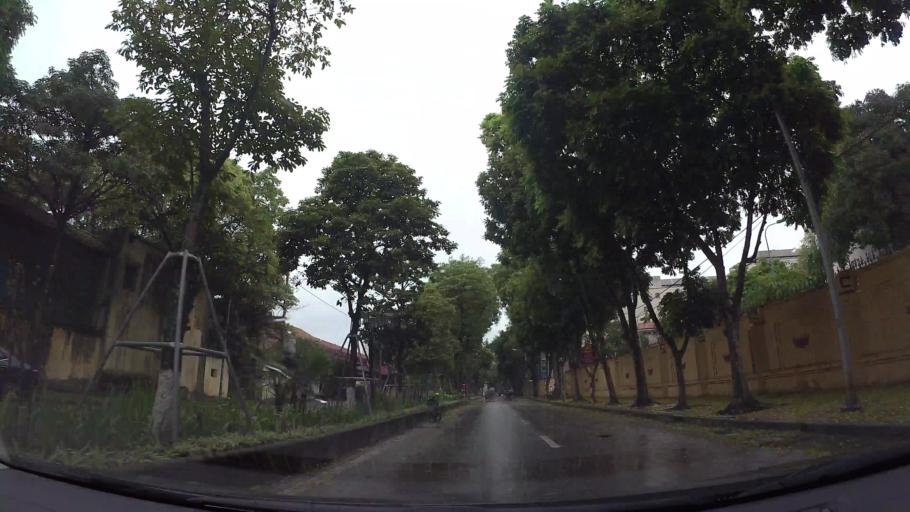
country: VN
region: Ha Noi
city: Hoan Kiem
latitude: 21.0389
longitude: 105.8417
